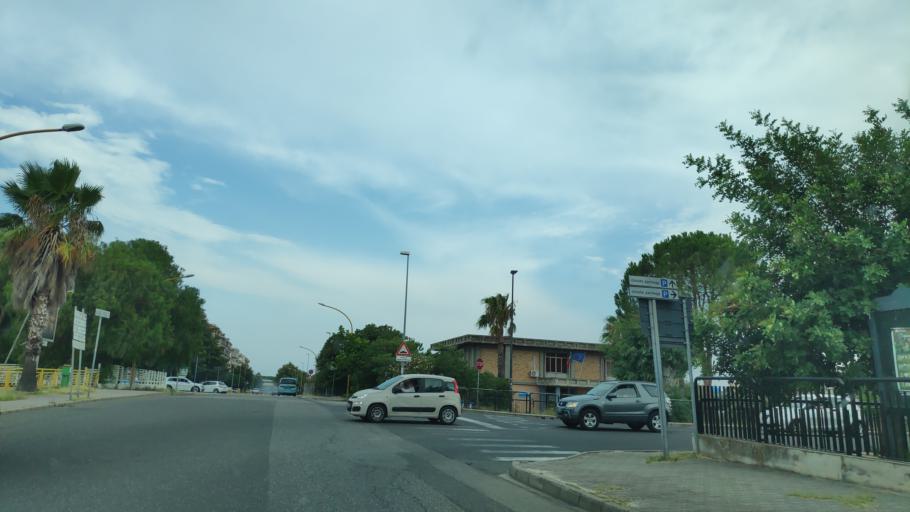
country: IT
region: Calabria
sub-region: Provincia di Catanzaro
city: Soverato Marina
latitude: 38.6847
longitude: 16.5512
